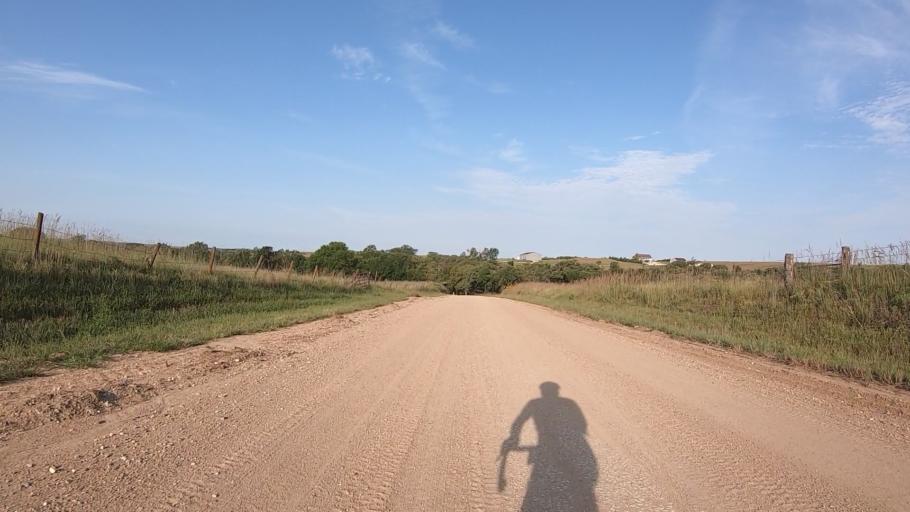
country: US
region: Kansas
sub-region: Marshall County
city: Blue Rapids
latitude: 39.6752
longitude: -96.7946
